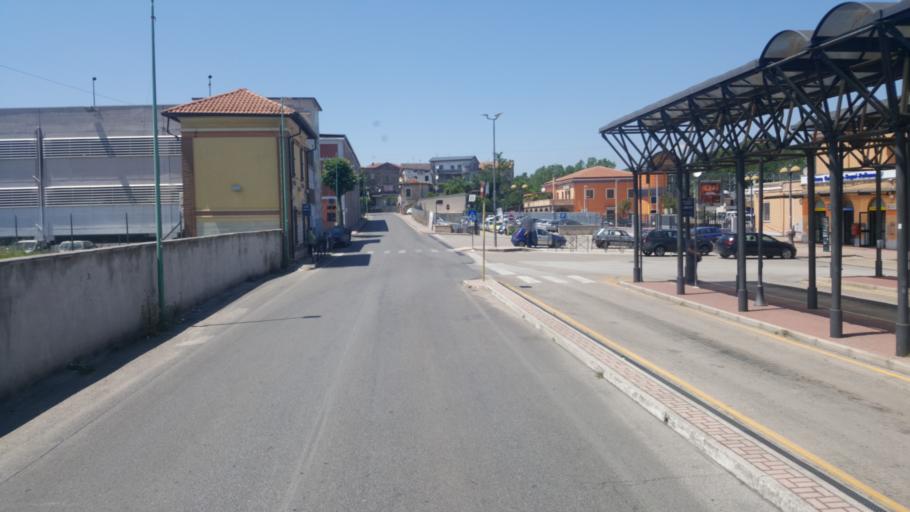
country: IT
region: Latium
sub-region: Citta metropolitana di Roma Capitale
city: Colleferro
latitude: 41.7395
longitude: 13.0029
